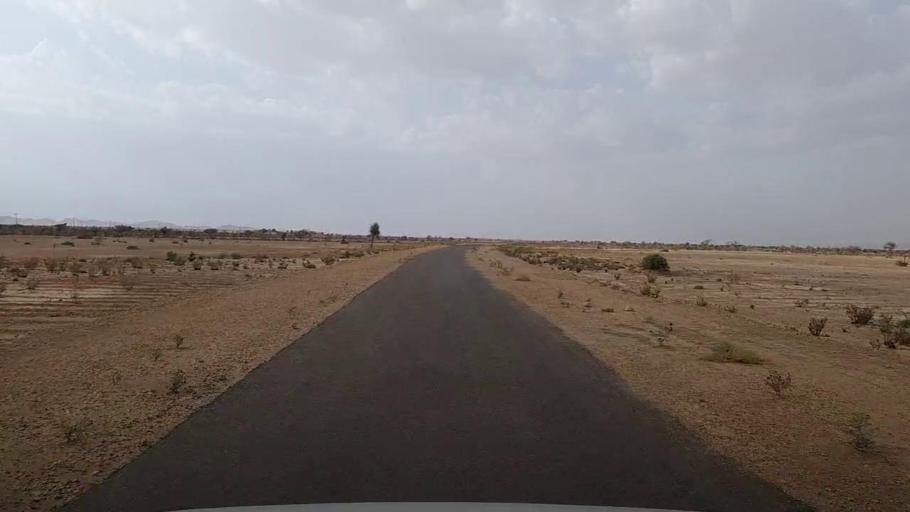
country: PK
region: Sindh
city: Jamshoro
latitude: 25.4516
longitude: 67.6781
